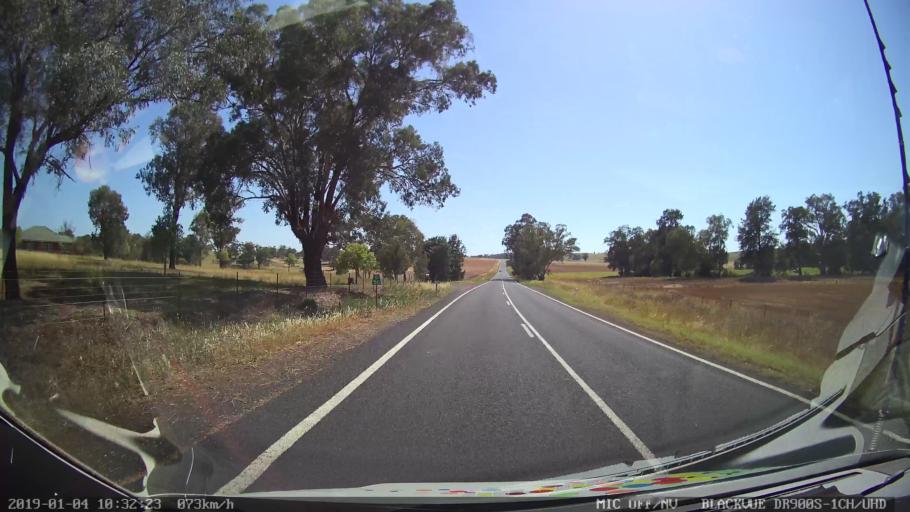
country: AU
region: New South Wales
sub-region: Cabonne
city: Canowindra
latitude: -33.3270
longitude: 148.6386
